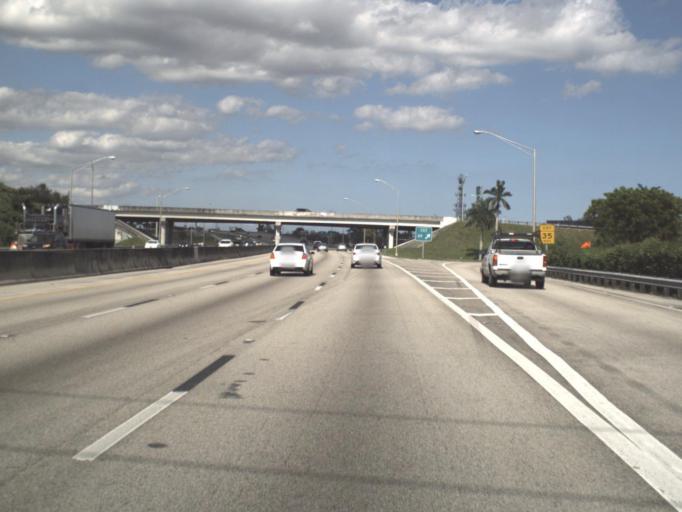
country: US
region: Florida
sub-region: Broward County
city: Pembroke Pines
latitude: 26.0039
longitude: -80.2158
